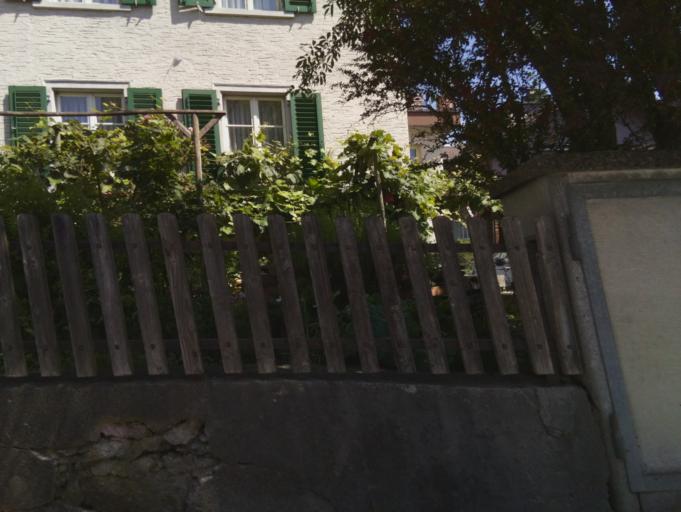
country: CH
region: Glarus
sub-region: Glarus
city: Nafels
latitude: 47.0980
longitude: 9.0597
